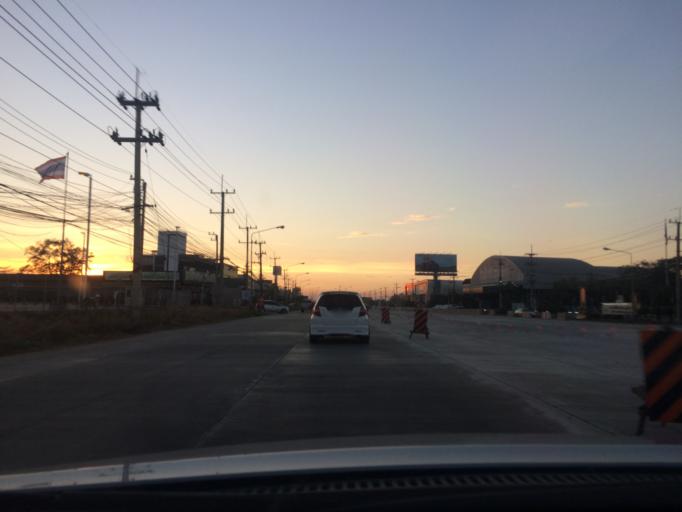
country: TH
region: Phitsanulok
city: Phitsanulok
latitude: 16.8173
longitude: 100.3229
